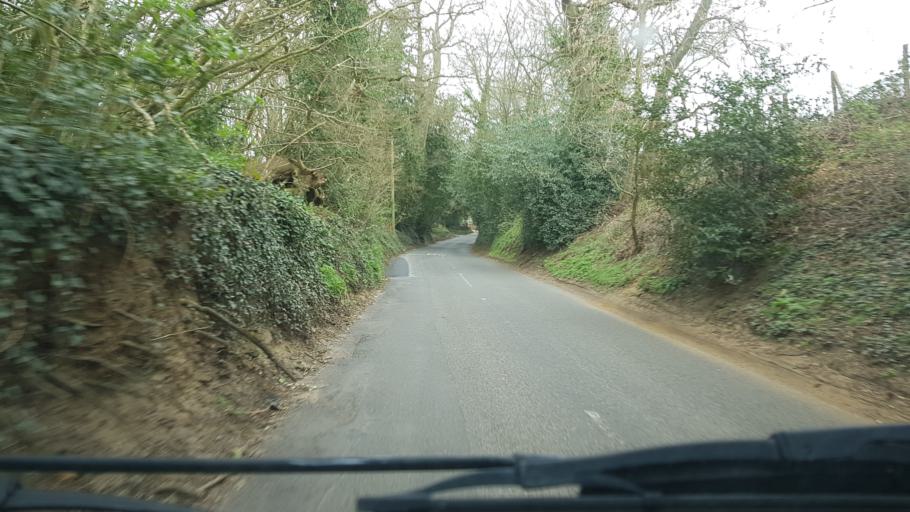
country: GB
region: England
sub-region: Surrey
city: Cranleigh
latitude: 51.2024
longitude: -0.4639
